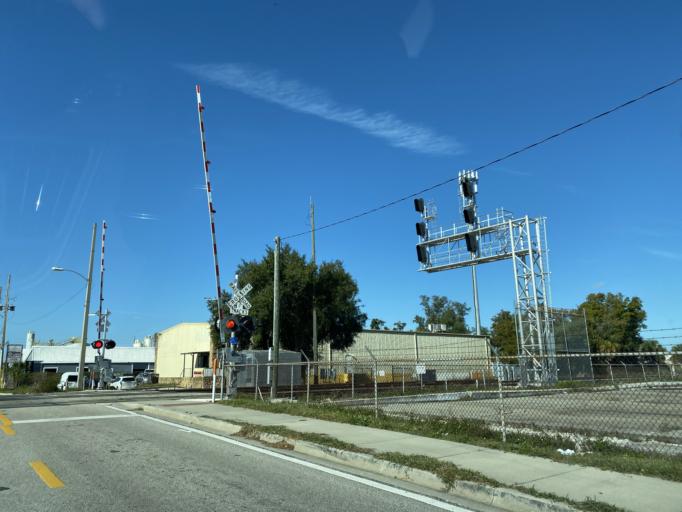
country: US
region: Florida
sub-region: Orange County
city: Holden Heights
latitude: 28.5166
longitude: -81.3807
